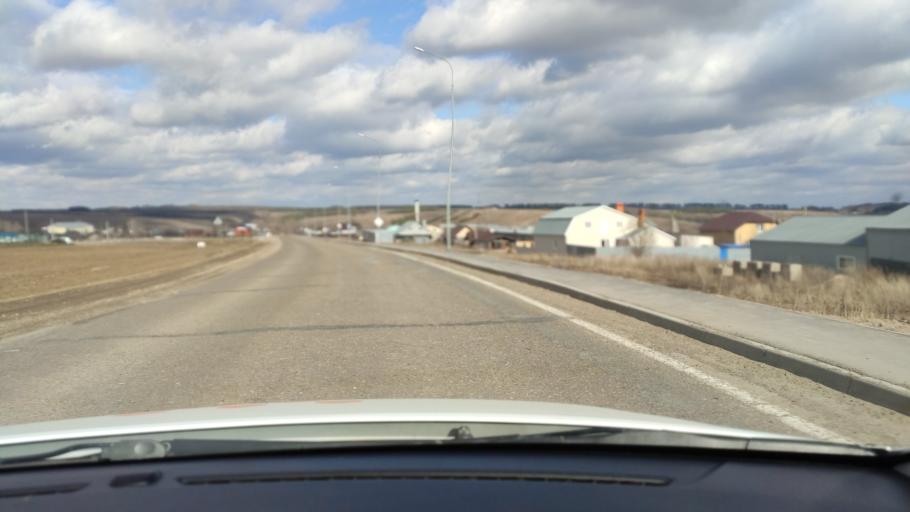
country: RU
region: Tatarstan
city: Vysokaya Gora
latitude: 56.1178
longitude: 49.1932
